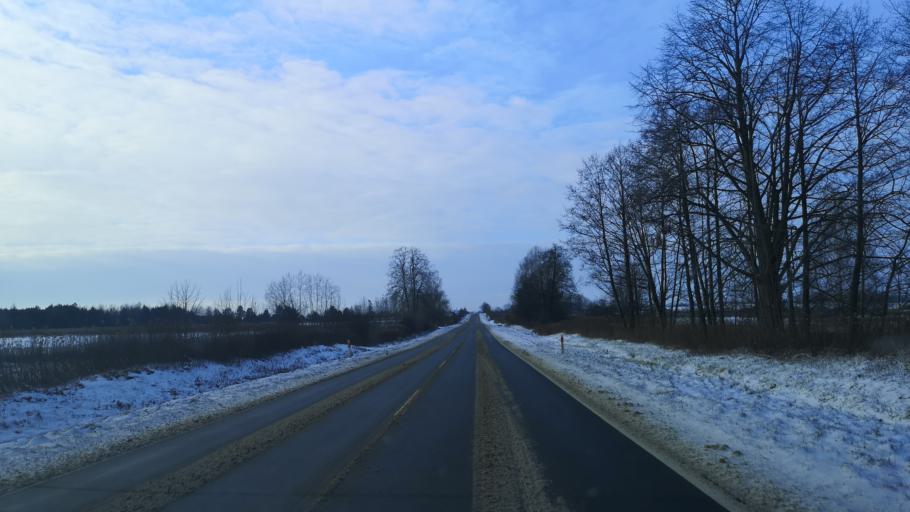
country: PL
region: Subcarpathian Voivodeship
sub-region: Powiat przeworski
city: Sieniawa
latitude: 50.2010
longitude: 22.6326
